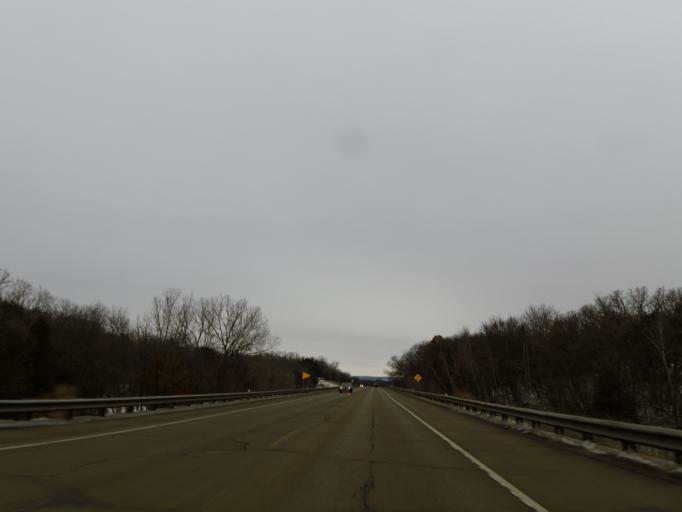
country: US
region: Wisconsin
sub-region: Saint Croix County
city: Hudson
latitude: 44.9735
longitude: -92.7748
